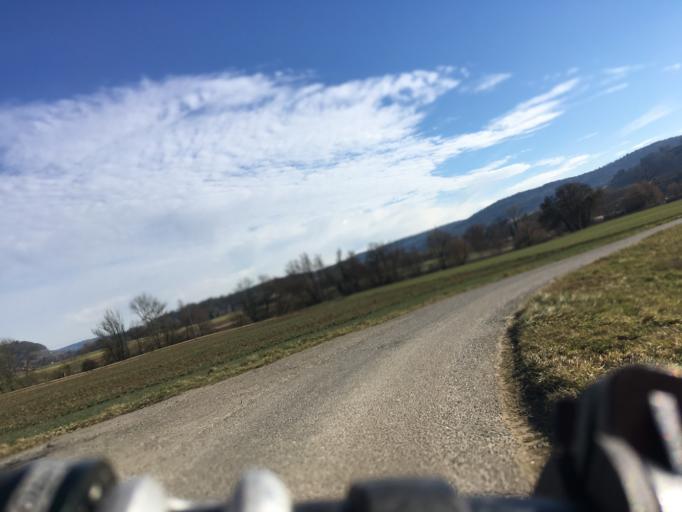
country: CH
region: Schaffhausen
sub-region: Bezirk Stein
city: Ramsen
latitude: 47.6846
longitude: 8.8063
